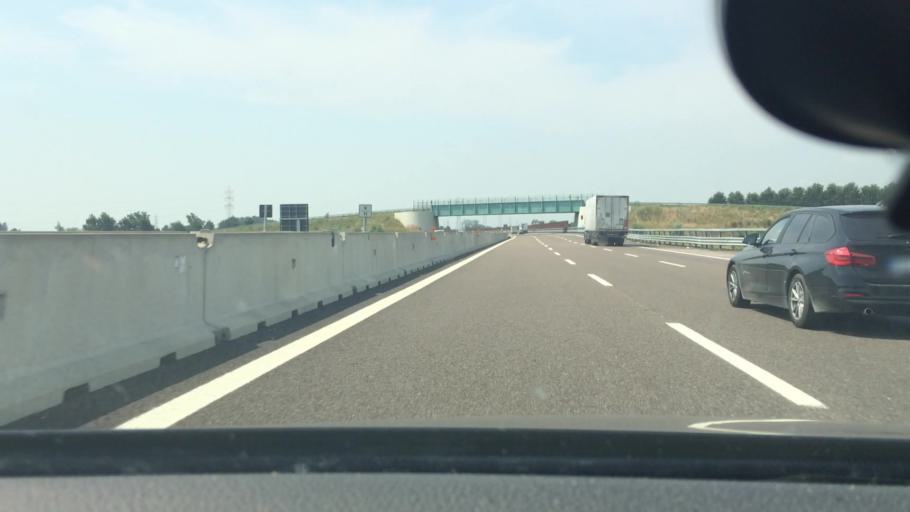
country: IT
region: Lombardy
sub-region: Citta metropolitana di Milano
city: Melzo
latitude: 45.4889
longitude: 9.4387
